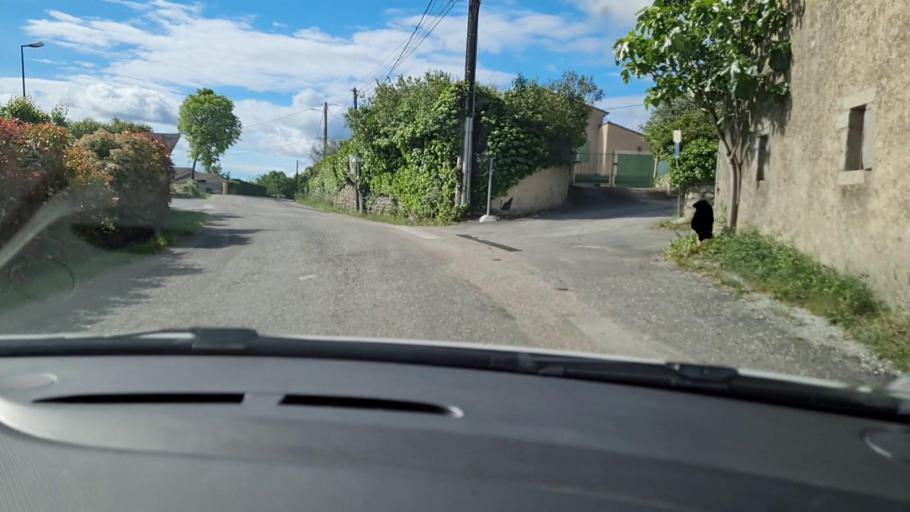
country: FR
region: Languedoc-Roussillon
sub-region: Departement du Gard
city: Sauve
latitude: 43.9884
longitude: 3.9513
